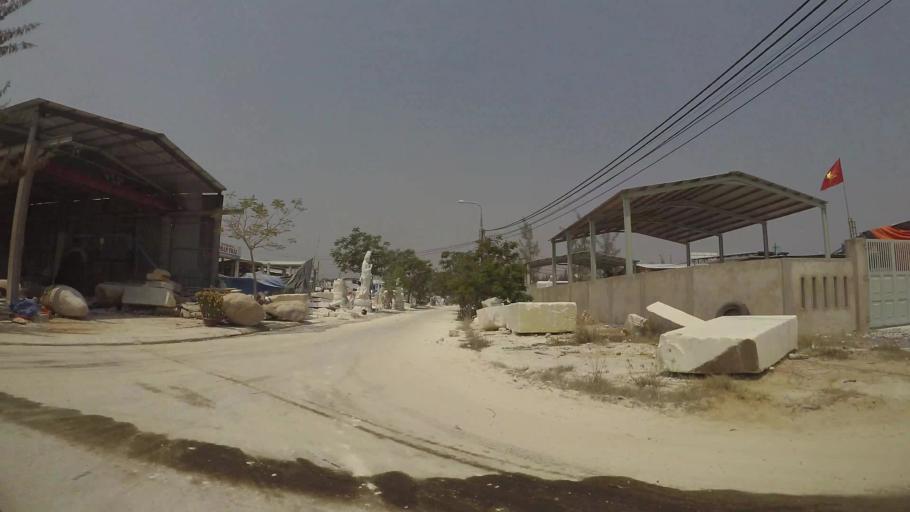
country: VN
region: Da Nang
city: Ngu Hanh Son
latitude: 15.9901
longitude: 108.2519
